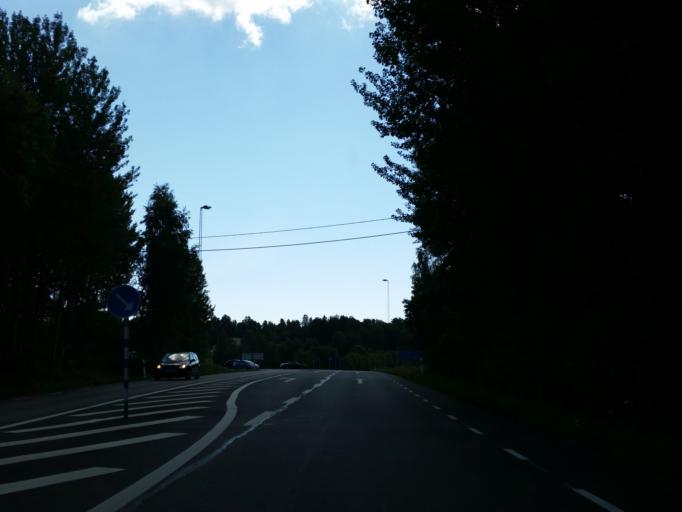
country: SE
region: Soedermanland
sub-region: Trosa Kommun
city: Vagnharad
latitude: 59.0065
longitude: 17.5966
